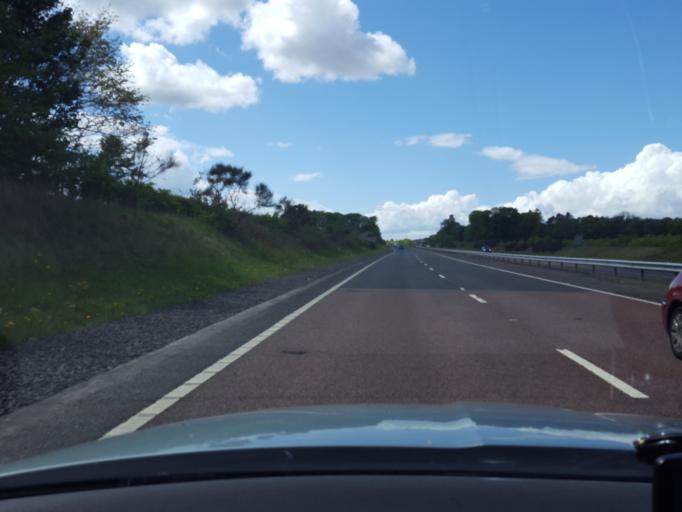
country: GB
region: Scotland
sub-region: Angus
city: Letham
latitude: 56.7144
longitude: -2.7924
